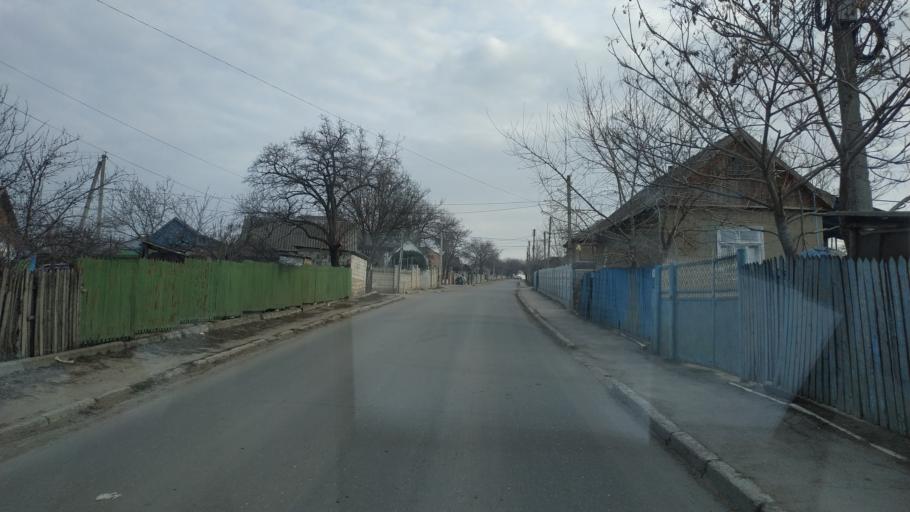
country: MD
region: Chisinau
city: Singera
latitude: 46.9662
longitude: 29.0607
